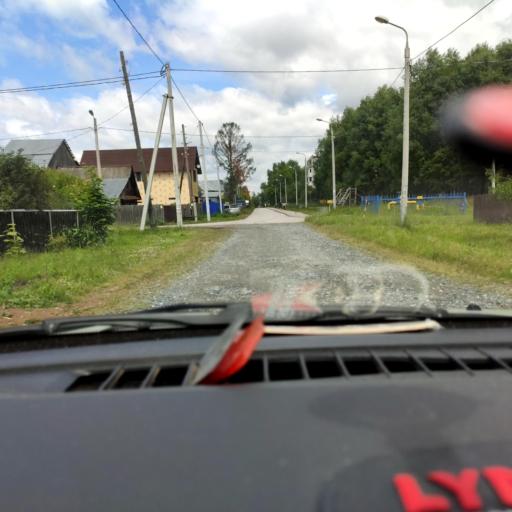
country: RU
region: Perm
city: Perm
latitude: 58.0765
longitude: 56.3581
